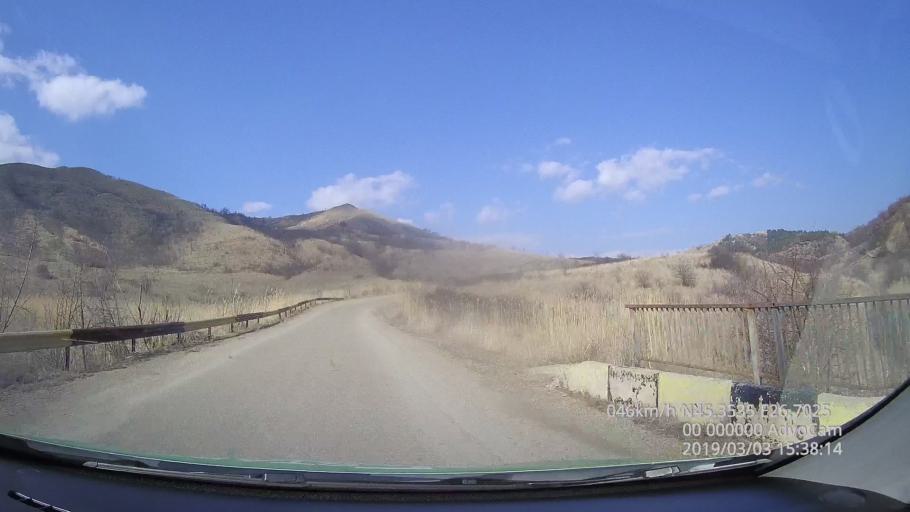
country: RO
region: Buzau
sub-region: Comuna Scortoasa
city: Scortoasa
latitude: 45.3538
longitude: 26.7024
